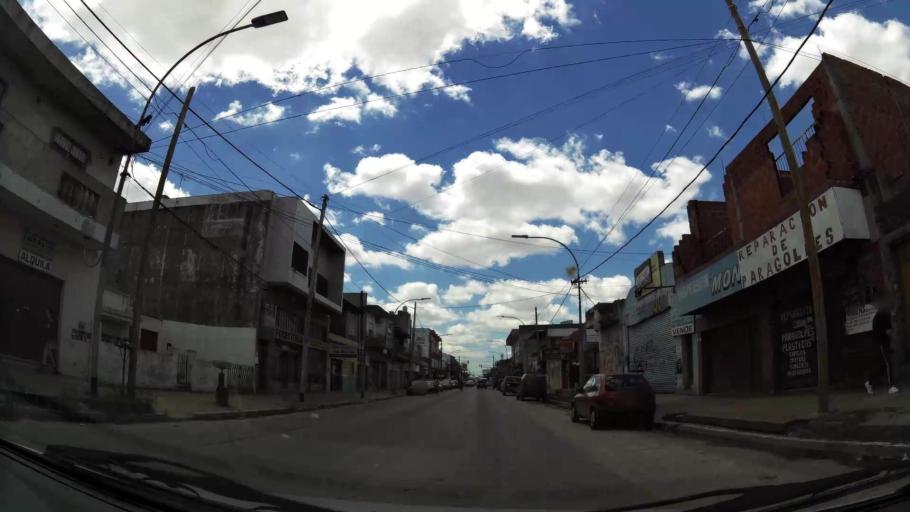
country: AR
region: Buenos Aires
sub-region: Partido de Lanus
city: Lanus
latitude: -34.7128
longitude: -58.4268
